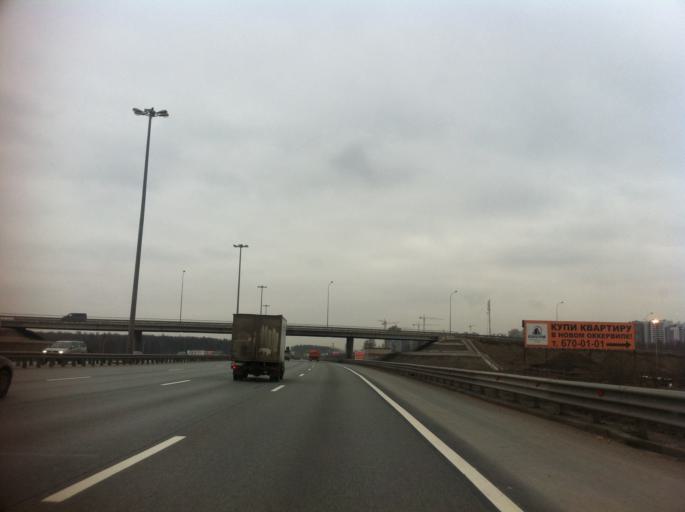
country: RU
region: St.-Petersburg
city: Krasnogvargeisky
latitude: 59.9173
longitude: 30.5255
